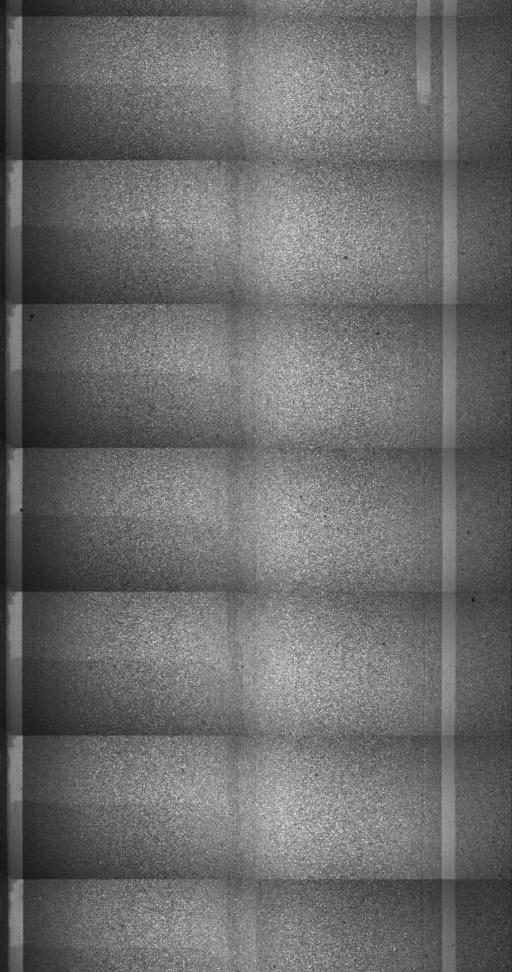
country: US
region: New York
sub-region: Washington County
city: Granville
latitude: 43.3611
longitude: -73.1845
